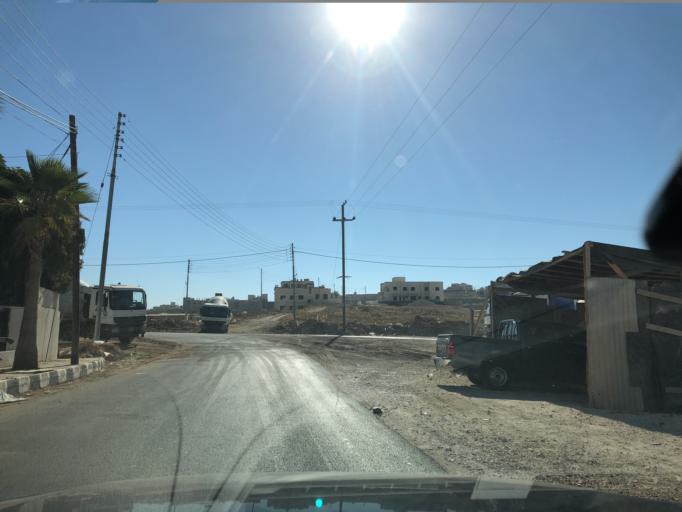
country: JO
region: Amman
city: Wadi as Sir
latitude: 31.9304
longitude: 35.8439
